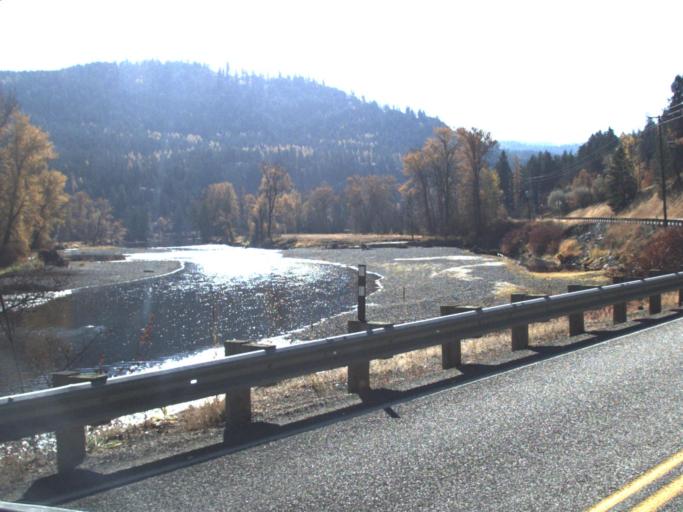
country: CA
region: British Columbia
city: Grand Forks
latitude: 48.9268
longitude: -118.5670
